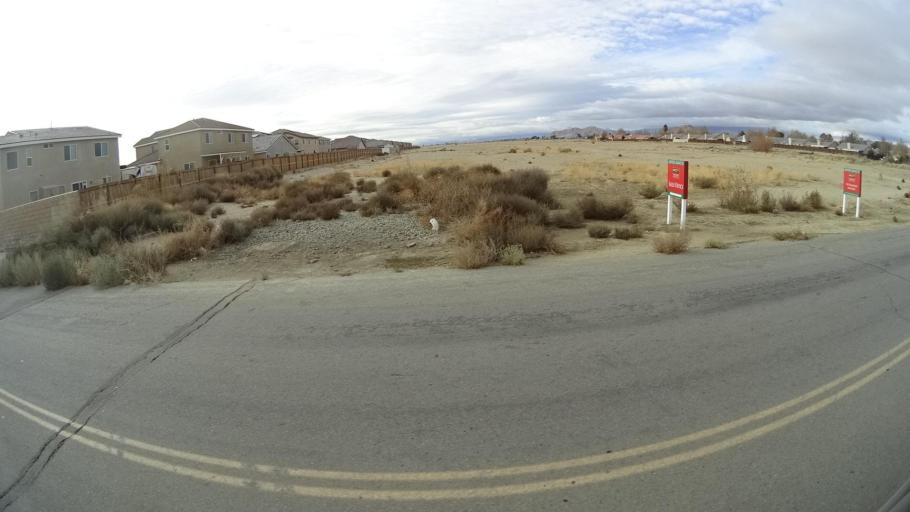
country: US
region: California
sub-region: Kern County
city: Rosamond
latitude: 34.8602
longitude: -118.1935
